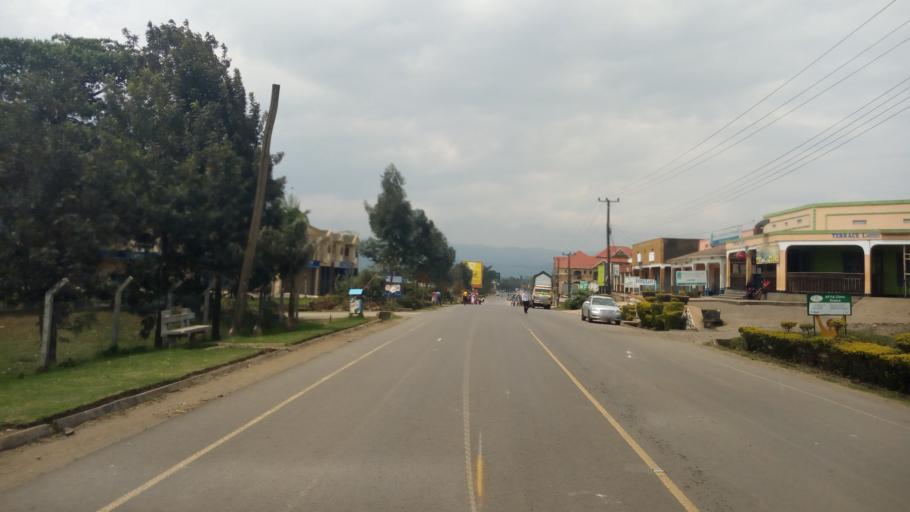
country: UG
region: Western Region
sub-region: Kisoro District
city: Kisoro
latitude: -1.2826
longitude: 29.6930
